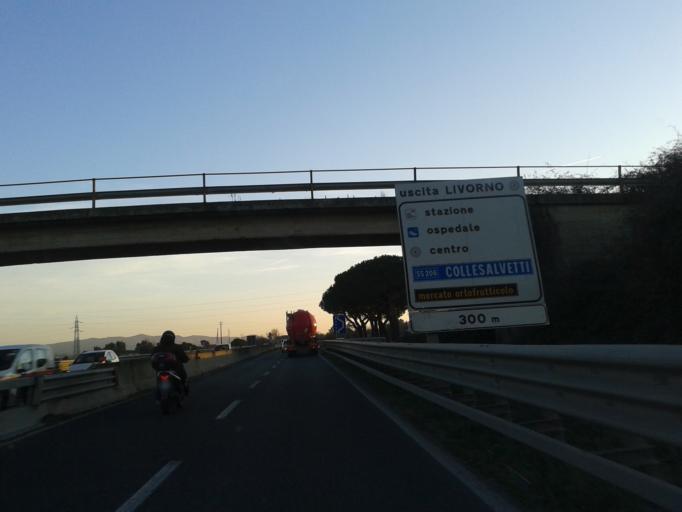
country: IT
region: Tuscany
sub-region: Provincia di Livorno
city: Livorno
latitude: 43.5667
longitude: 10.3469
